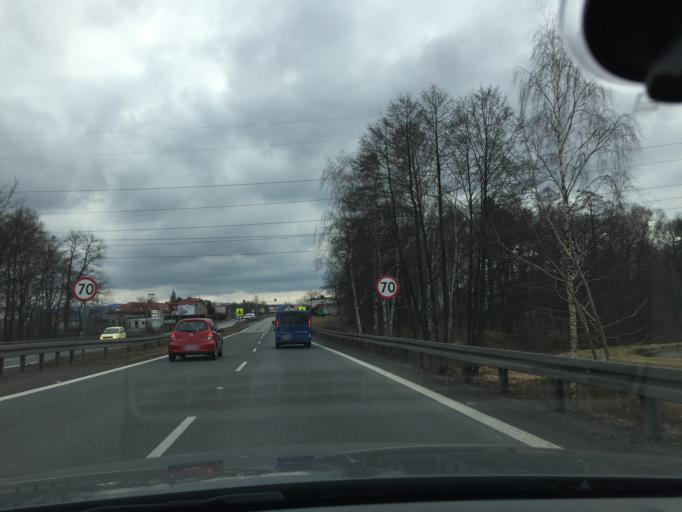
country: PL
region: Silesian Voivodeship
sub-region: Powiat bielski
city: Mazancowice
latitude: 49.8655
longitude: 19.0119
